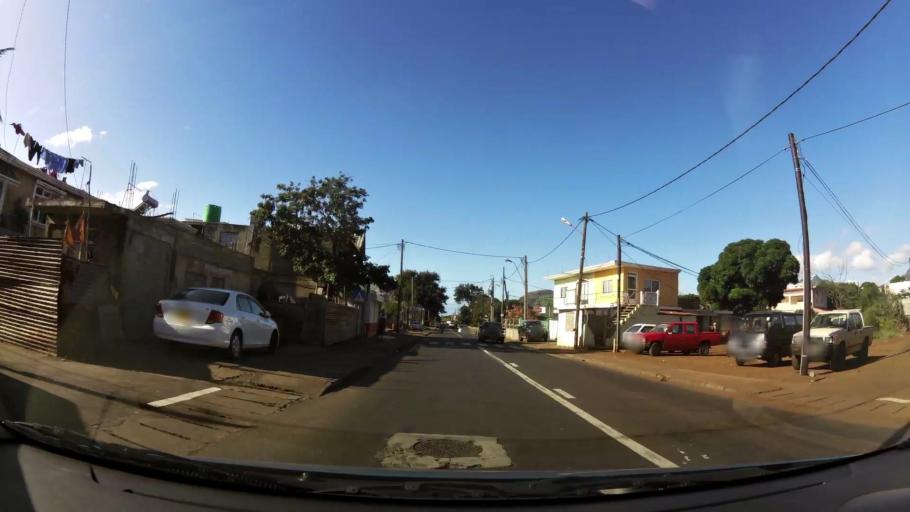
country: MU
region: Black River
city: Petite Riviere
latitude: -20.1854
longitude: 57.4611
